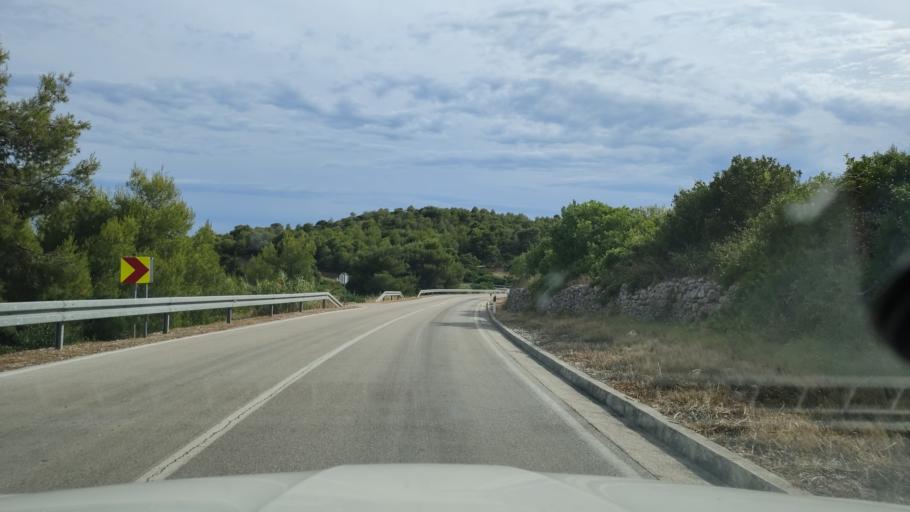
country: HR
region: Splitsko-Dalmatinska
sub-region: Grad Vis
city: Vis
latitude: 43.0349
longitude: 16.2025
